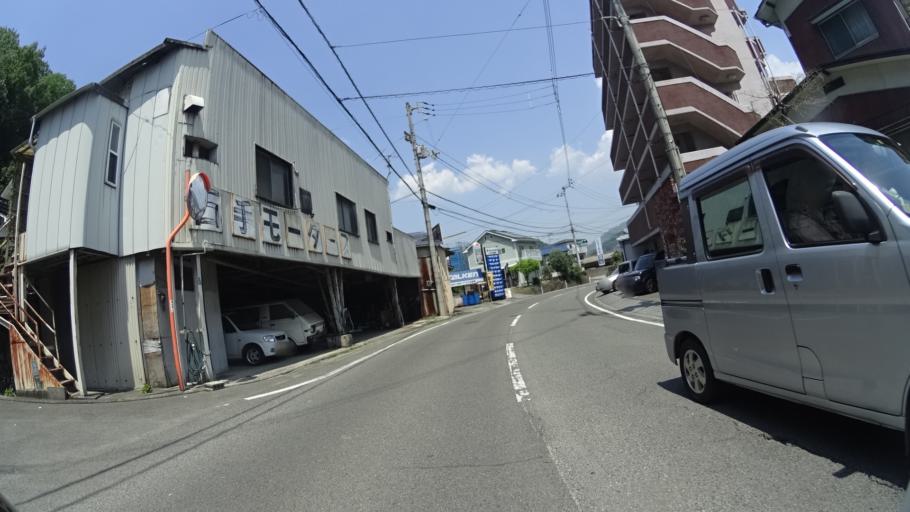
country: JP
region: Ehime
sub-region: Shikoku-chuo Shi
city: Matsuyama
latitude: 33.8486
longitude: 132.7996
